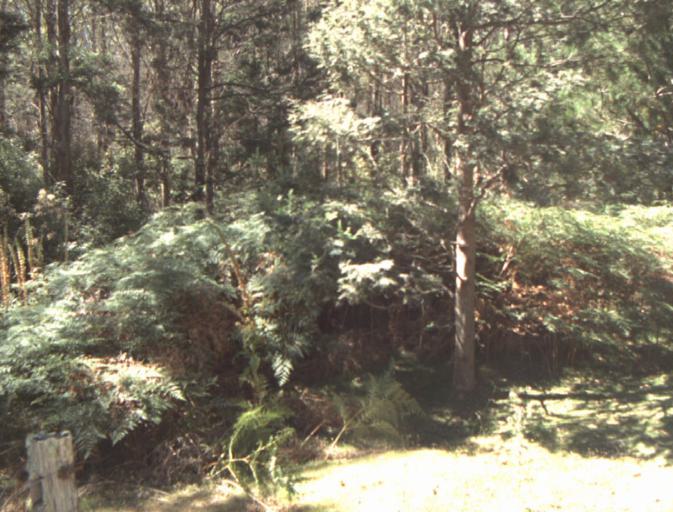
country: AU
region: Tasmania
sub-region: Dorset
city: Scottsdale
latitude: -41.2572
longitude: 147.3465
